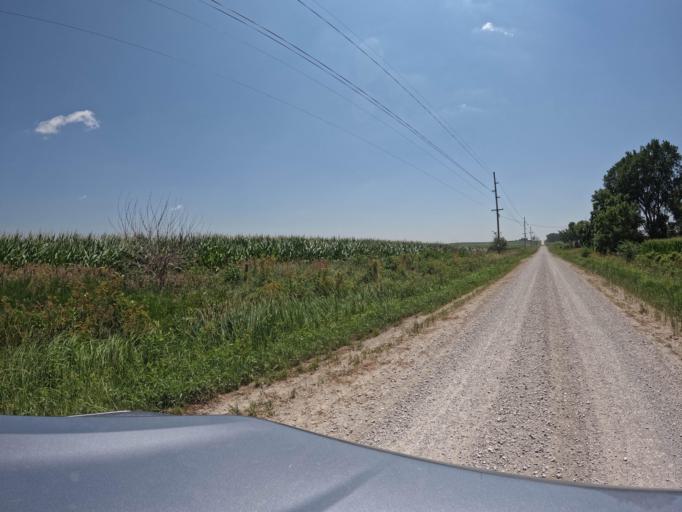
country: US
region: Iowa
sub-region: Keokuk County
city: Sigourney
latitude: 41.2910
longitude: -92.1807
